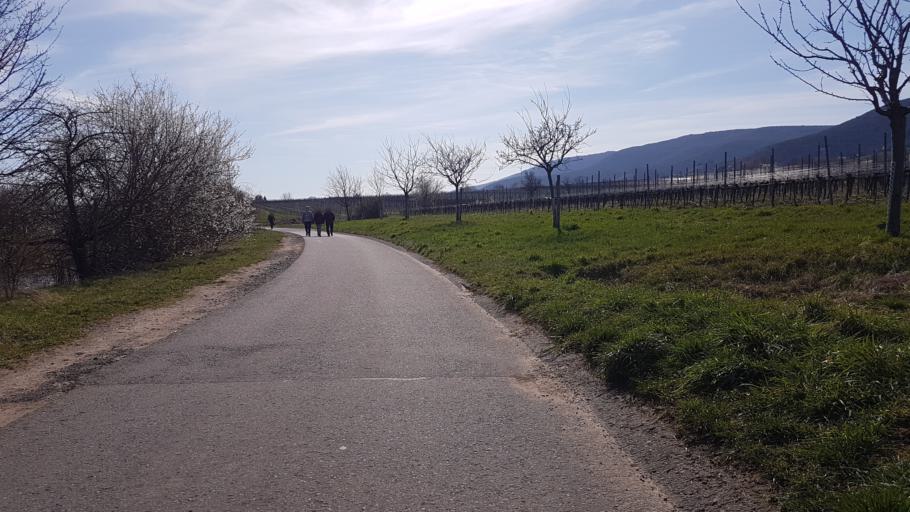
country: DE
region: Rheinland-Pfalz
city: Maikammer
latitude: 49.3176
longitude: 8.1291
